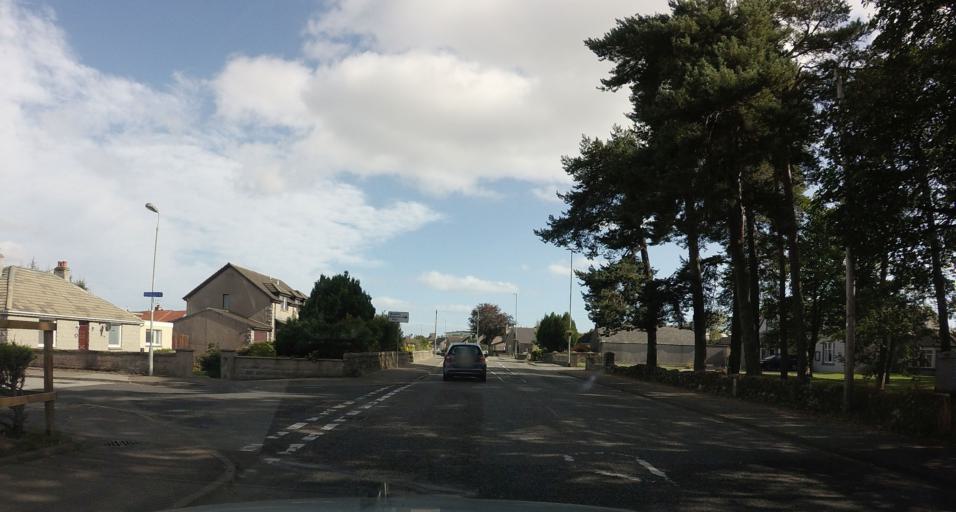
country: GB
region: Scotland
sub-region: Aberdeenshire
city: Westhill
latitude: 57.1505
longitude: -2.3006
